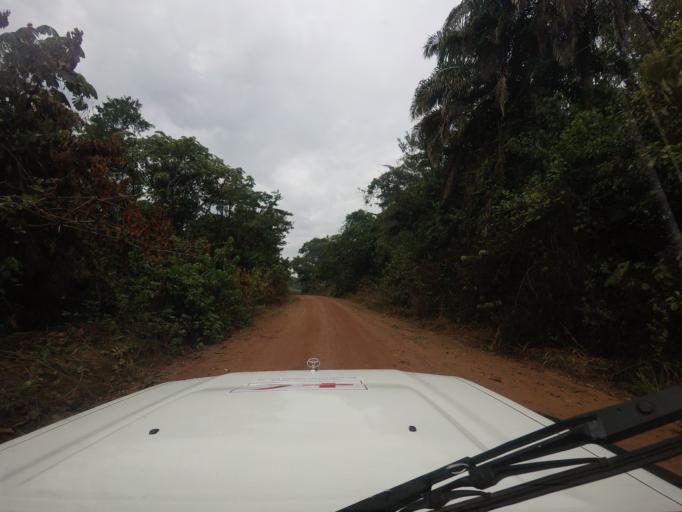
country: SL
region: Eastern Province
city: Buedu
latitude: 8.3258
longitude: -10.1596
